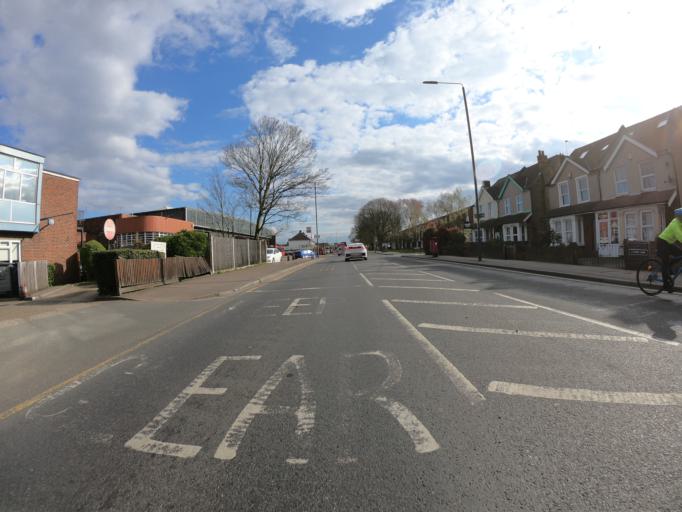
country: GB
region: England
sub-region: Greater London
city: Bexleyheath
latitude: 51.4609
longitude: 0.1532
